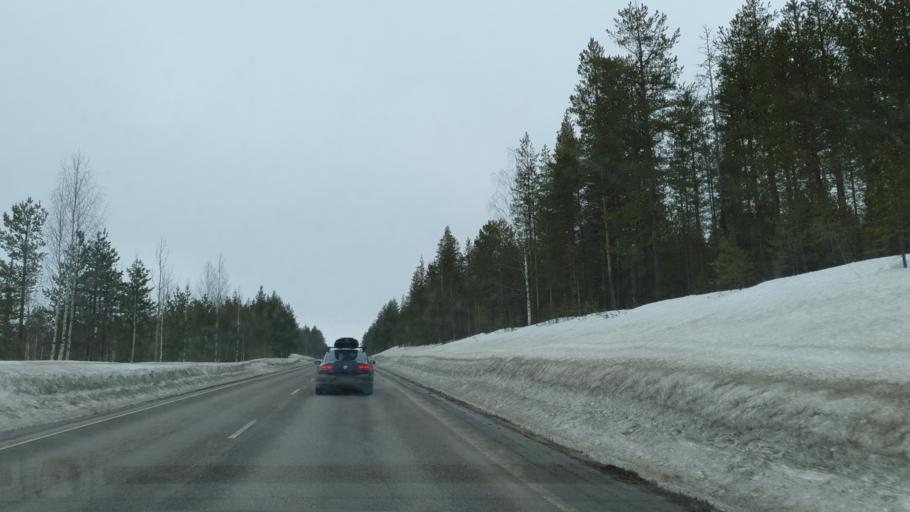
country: FI
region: Lapland
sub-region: Torniolaakso
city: Pello
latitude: 66.8569
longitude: 24.0465
